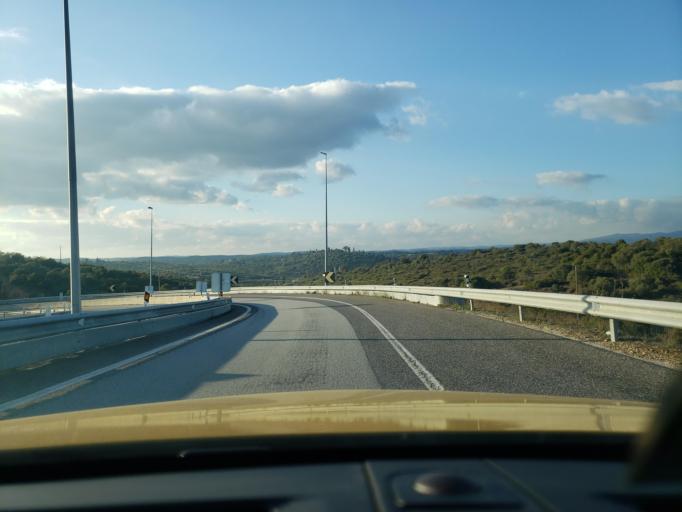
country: PT
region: Faro
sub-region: Portimao
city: Portimao
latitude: 37.1768
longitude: -8.5668
